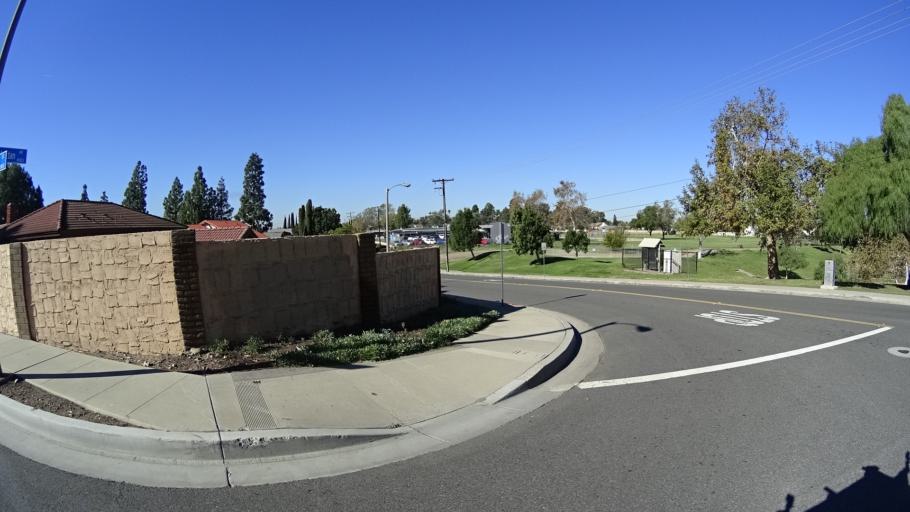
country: US
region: California
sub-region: Orange County
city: North Tustin
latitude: 33.7788
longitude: -117.8053
